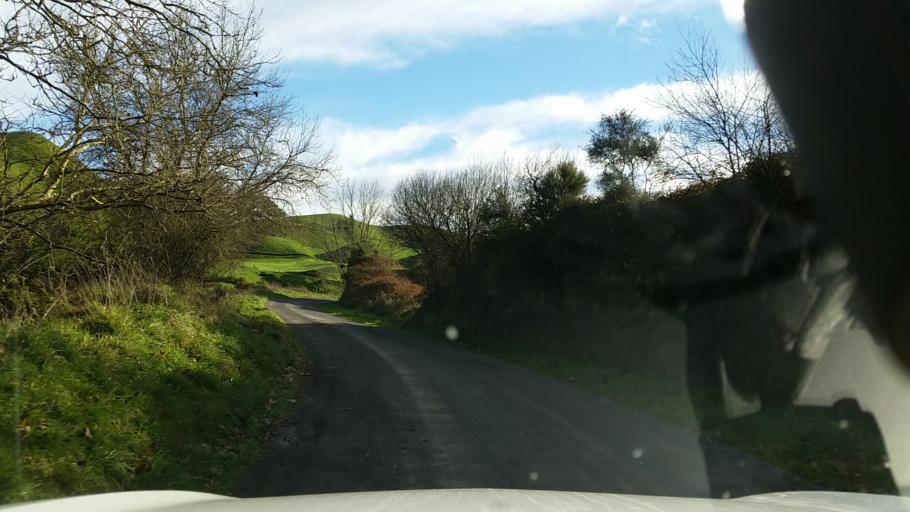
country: NZ
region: Waikato
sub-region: South Waikato District
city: Tokoroa
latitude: -38.3730
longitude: 176.0869
